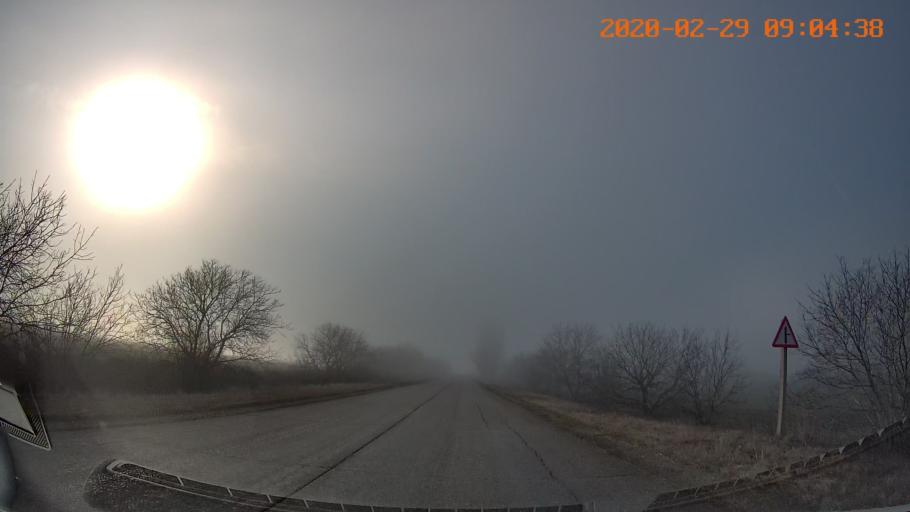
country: MD
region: Telenesti
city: Tiraspolul Nou
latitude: 46.8996
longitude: 29.7370
